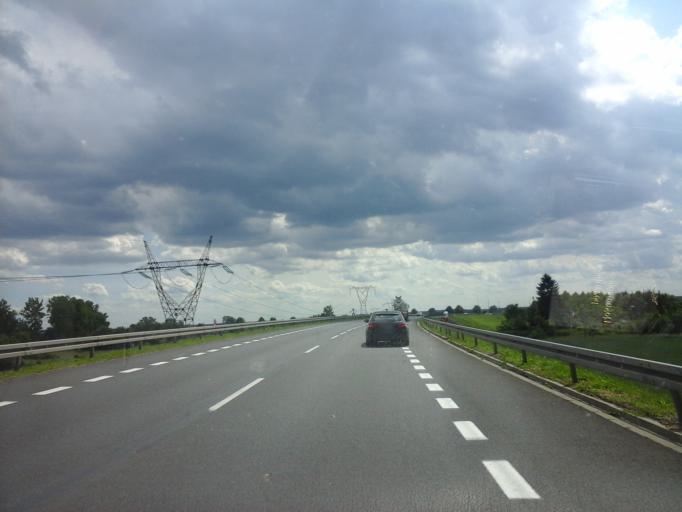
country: PL
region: West Pomeranian Voivodeship
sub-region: Powiat bialogardzki
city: Karlino
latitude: 54.0358
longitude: 15.8968
